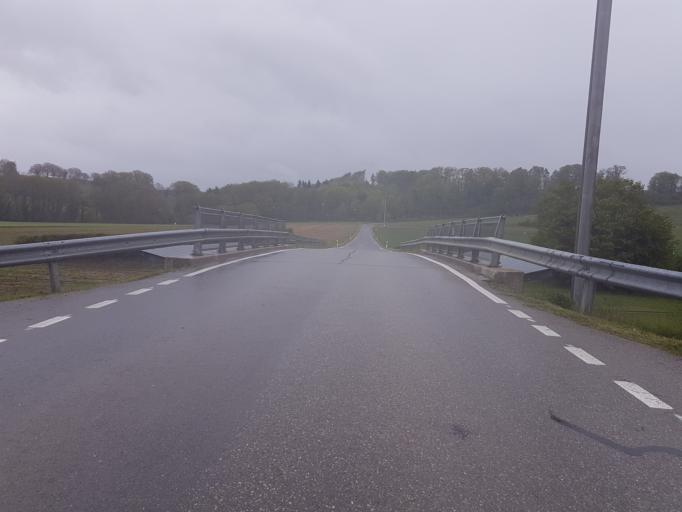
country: CH
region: Vaud
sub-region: Gros-de-Vaud District
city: Penthalaz
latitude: 46.6244
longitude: 6.5279
